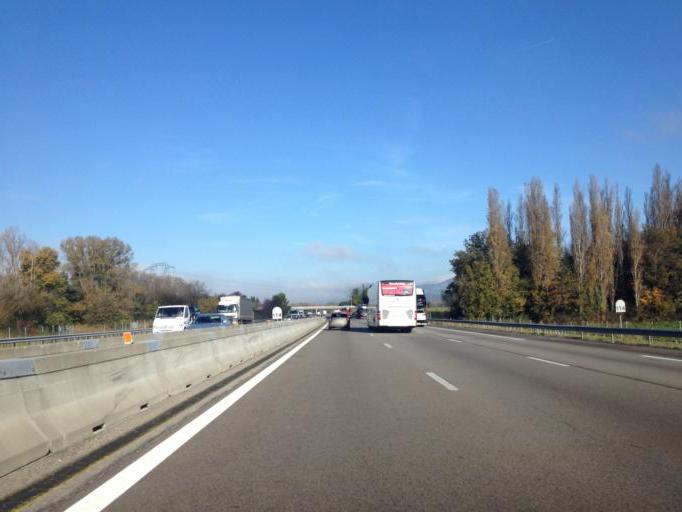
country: FR
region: Rhone-Alpes
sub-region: Departement de la Drome
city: Montboucher-sur-Jabron
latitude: 44.5666
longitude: 4.8104
